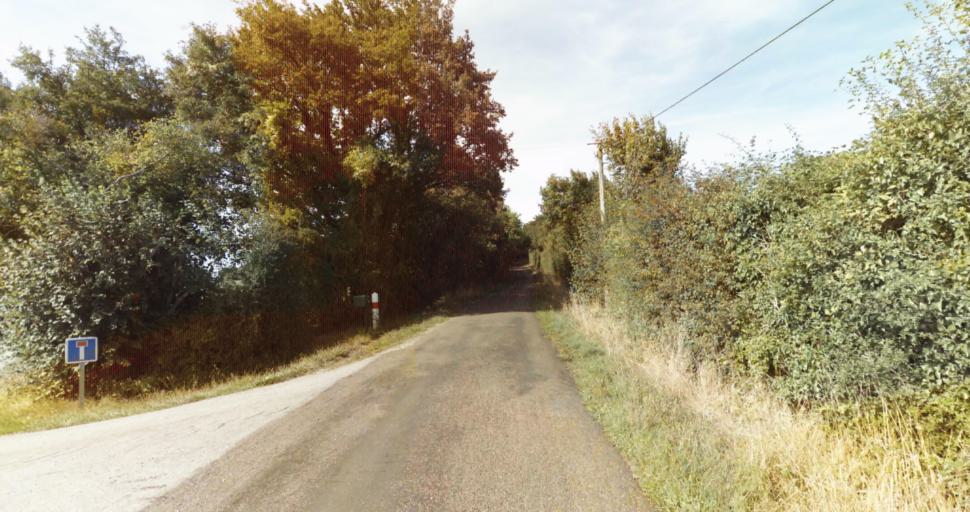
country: FR
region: Lower Normandy
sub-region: Departement de l'Orne
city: Sees
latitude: 48.7089
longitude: 0.1764
